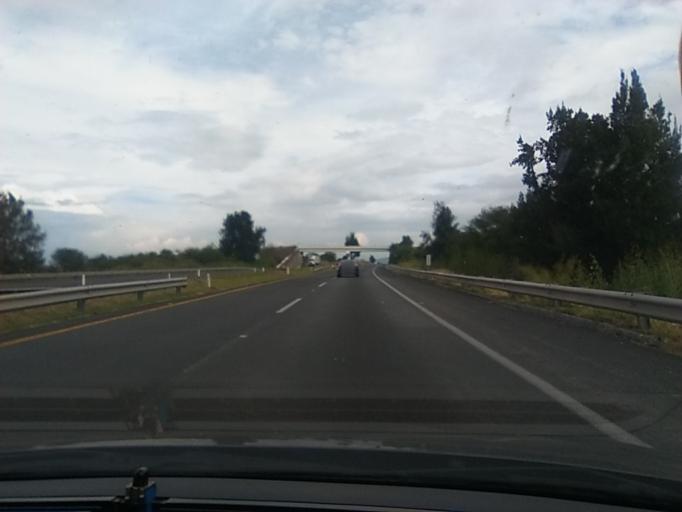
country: MX
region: Michoacan
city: Vistahermosa de Negrete
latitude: 20.2808
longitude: -102.4561
